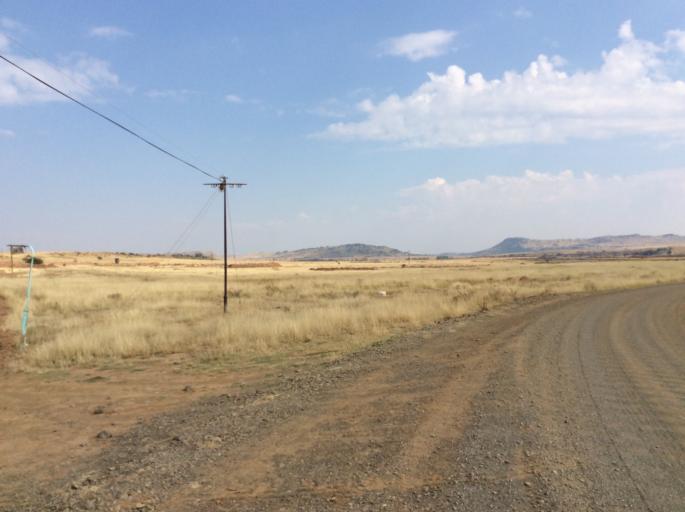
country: LS
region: Mafeteng
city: Mafeteng
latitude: -29.9907
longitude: 26.9999
